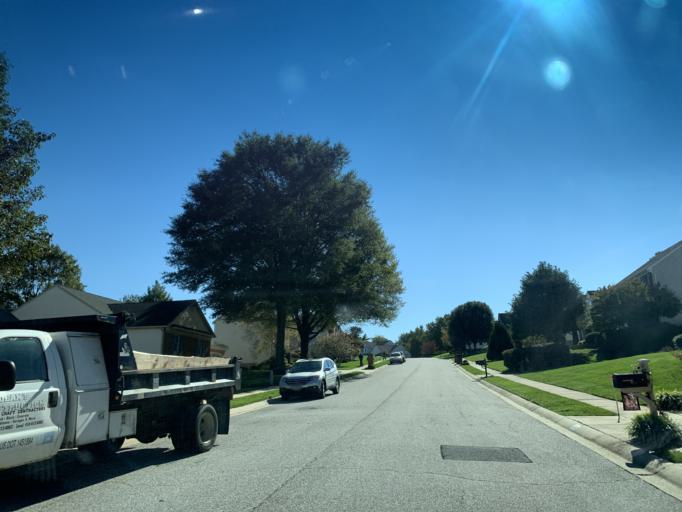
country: US
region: Maryland
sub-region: Harford County
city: Bel Air South
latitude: 39.5126
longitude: -76.3219
